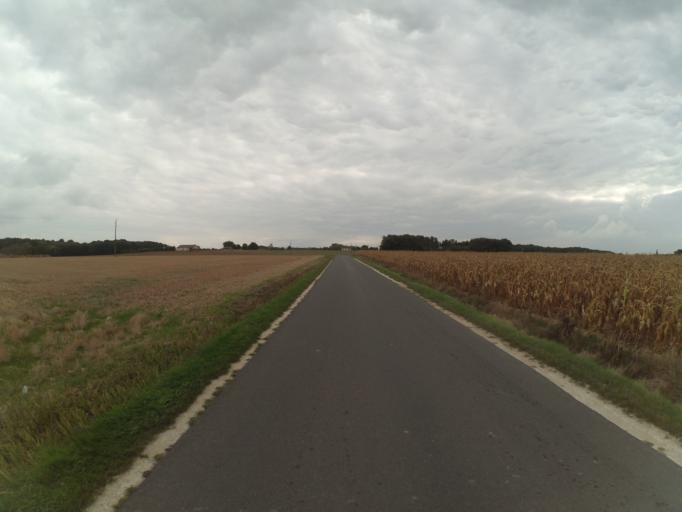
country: FR
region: Centre
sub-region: Departement d'Indre-et-Loire
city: Auzouer-en-Touraine
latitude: 47.5010
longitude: 0.9274
